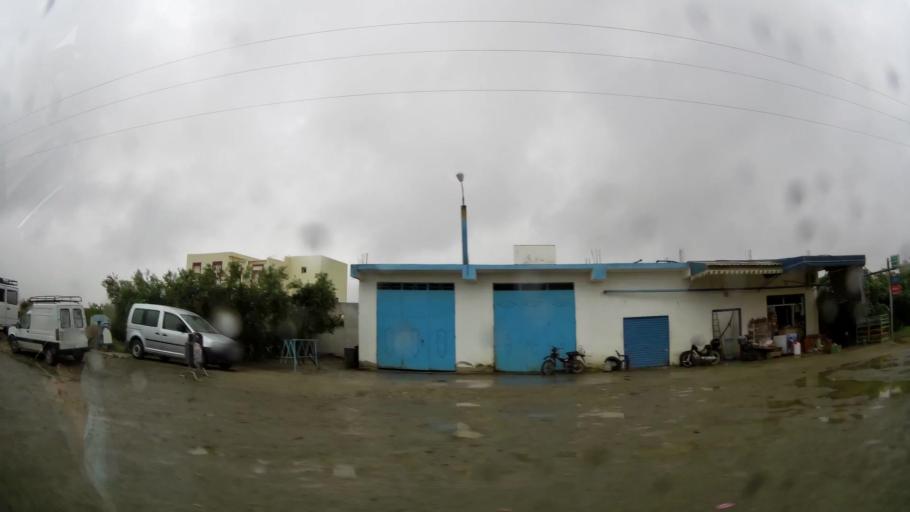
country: MA
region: Taza-Al Hoceima-Taounate
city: Imzourene
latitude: 35.1411
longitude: -3.8012
